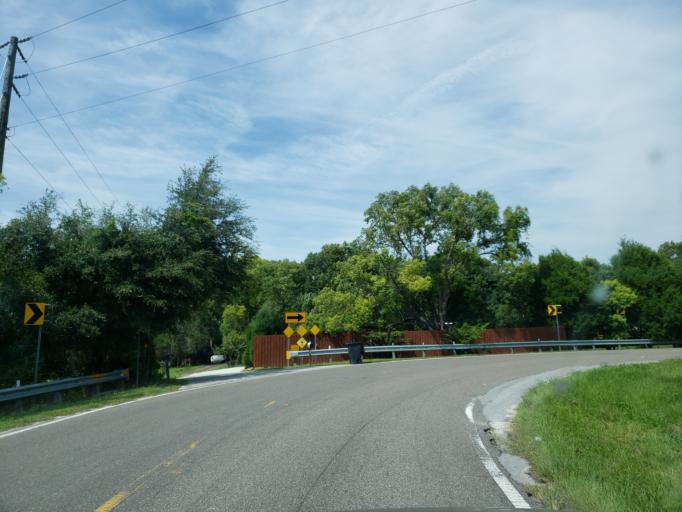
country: US
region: Florida
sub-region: Pasco County
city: Wesley Chapel
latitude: 28.2763
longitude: -82.3203
